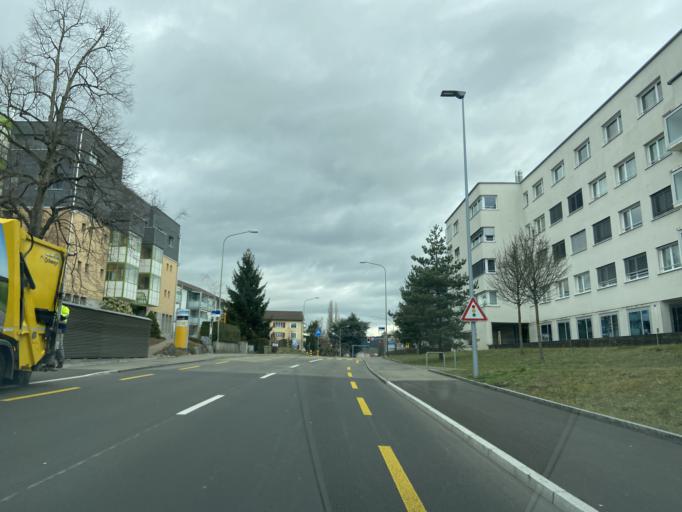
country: CH
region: Zurich
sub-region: Bezirk Buelach
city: Kloten / Holberg
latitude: 47.4435
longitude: 8.5781
